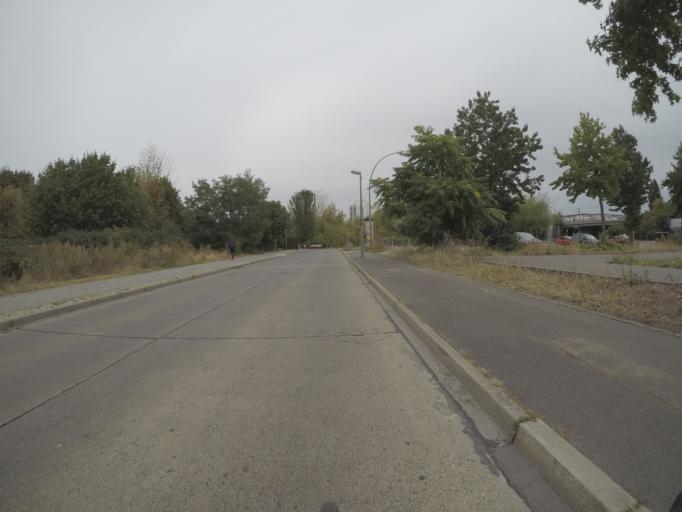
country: DE
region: Berlin
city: Neu-Hohenschoenhausen
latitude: 52.5662
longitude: 13.5104
